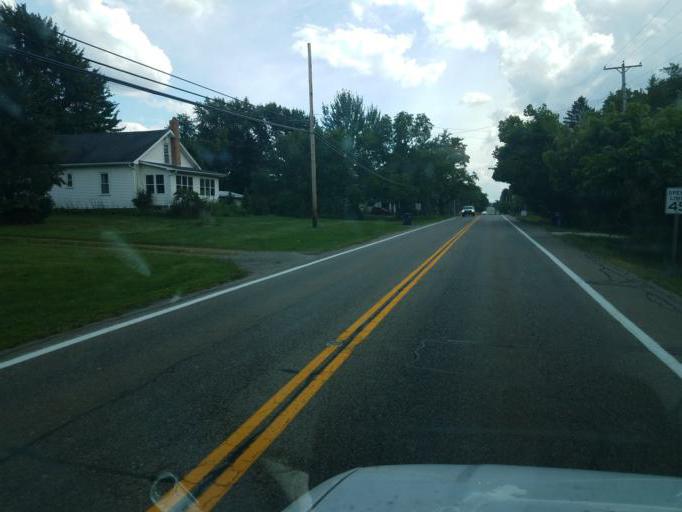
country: US
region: Ohio
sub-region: Portage County
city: Ravenna
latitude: 41.0843
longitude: -81.2431
